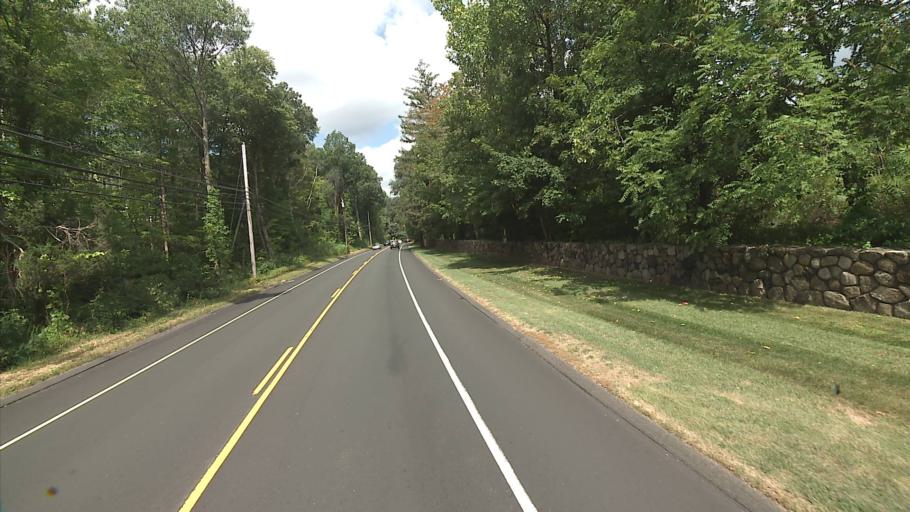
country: US
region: Connecticut
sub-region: Hartford County
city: Weatogue
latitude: 41.8338
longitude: -72.7777
